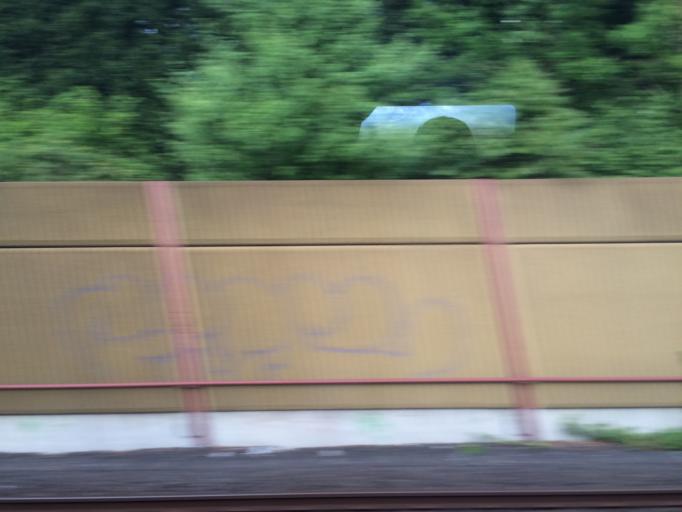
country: DE
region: North Rhine-Westphalia
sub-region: Regierungsbezirk Koln
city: Leverkusen
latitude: 51.0429
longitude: 6.9889
